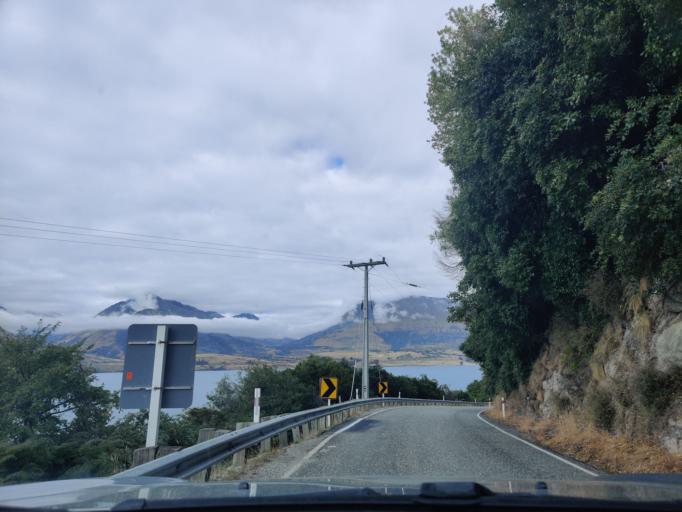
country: NZ
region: Otago
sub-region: Queenstown-Lakes District
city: Queenstown
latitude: -45.0795
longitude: 168.4814
